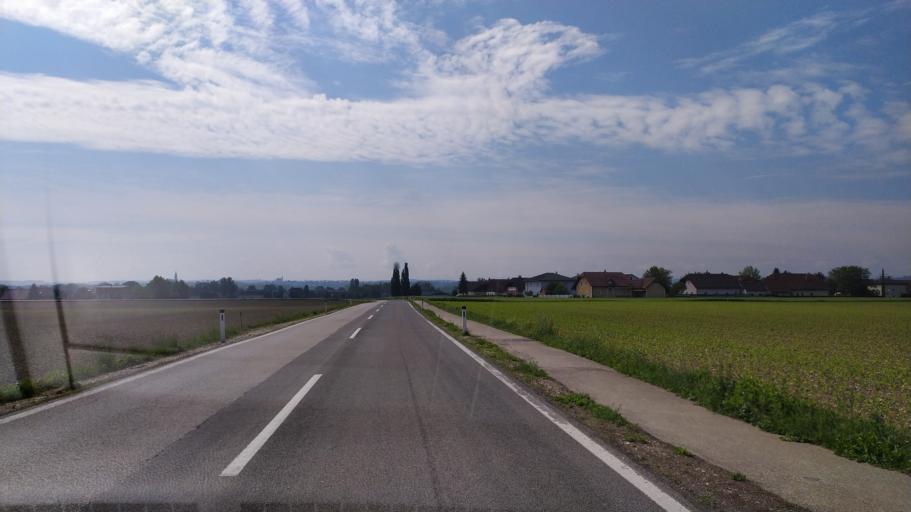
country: AT
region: Upper Austria
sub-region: Politischer Bezirk Perg
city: Perg
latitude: 48.1932
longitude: 14.6909
